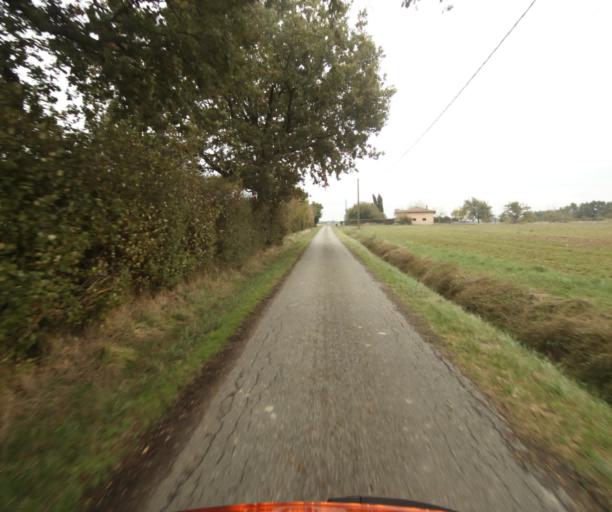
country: FR
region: Midi-Pyrenees
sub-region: Departement de la Haute-Garonne
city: Launac
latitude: 43.8044
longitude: 1.1914
